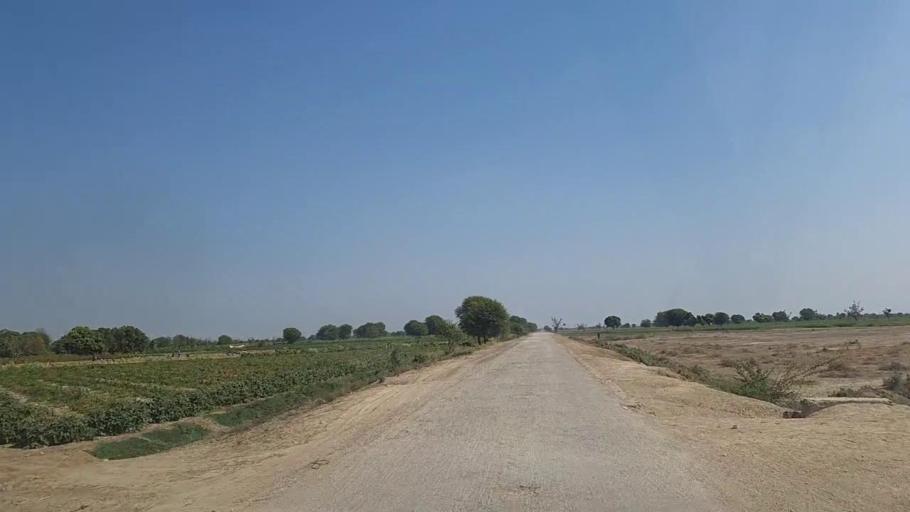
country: PK
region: Sindh
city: Digri
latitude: 25.1673
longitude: 69.1420
